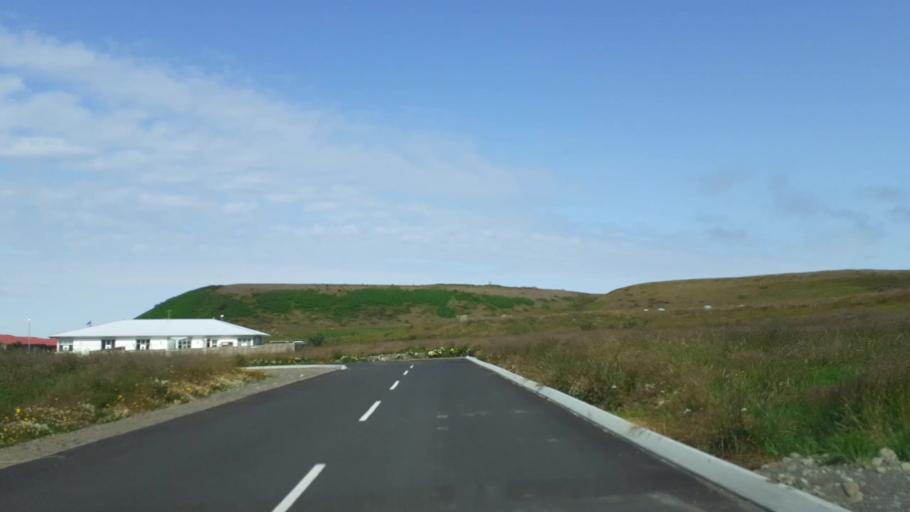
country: IS
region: Northwest
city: Saudarkrokur
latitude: 65.6642
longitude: -20.2843
